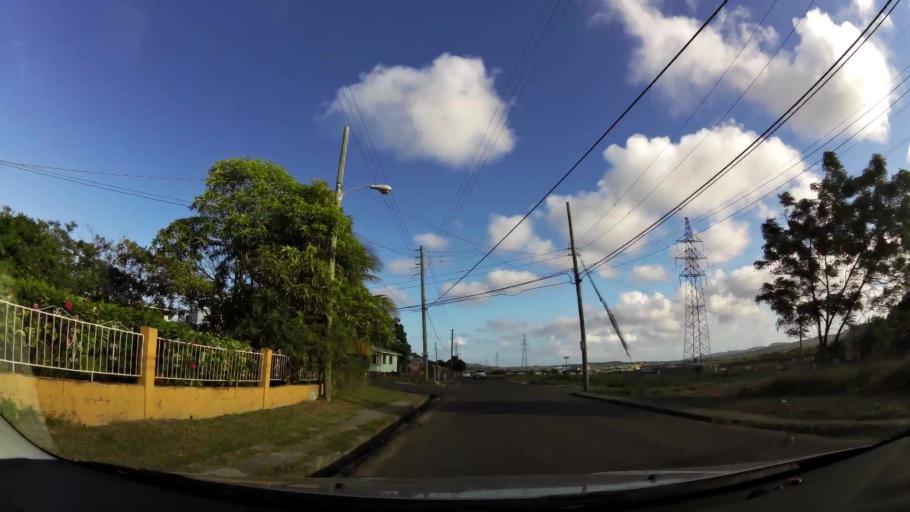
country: AG
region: Saint George
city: Piggotts
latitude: 17.1203
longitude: -61.8006
